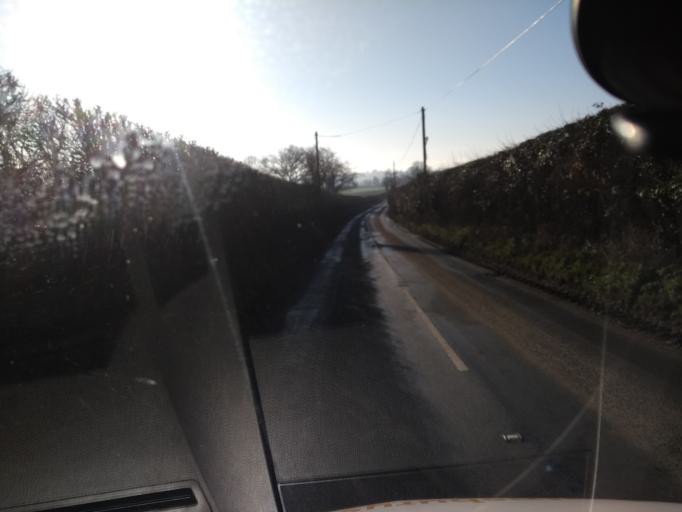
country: GB
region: England
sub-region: Somerset
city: Redlynch
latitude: 51.0800
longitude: -2.4129
